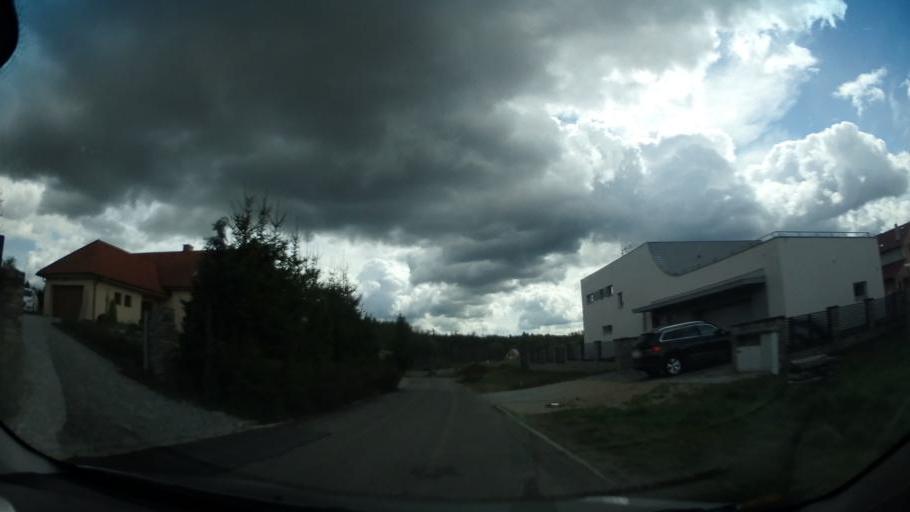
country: CZ
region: Vysocina
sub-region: Okres Zd'ar nad Sazavou
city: Velka Bites
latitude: 49.2935
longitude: 16.2299
